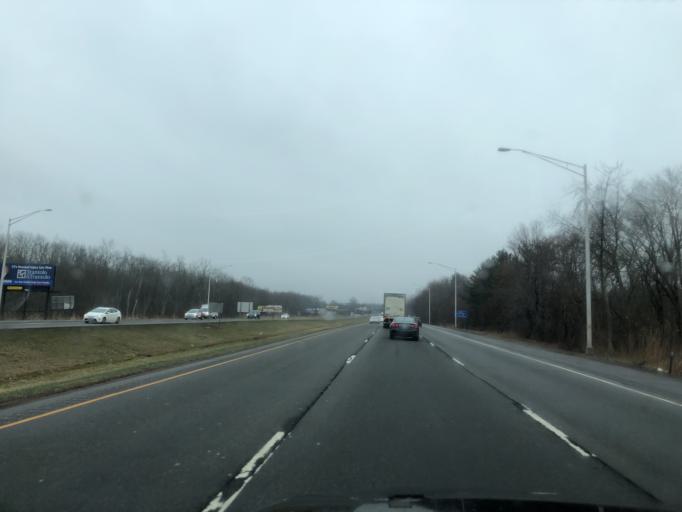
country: US
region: Connecticut
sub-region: New Haven County
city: Meriden
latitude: 41.5187
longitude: -72.7713
